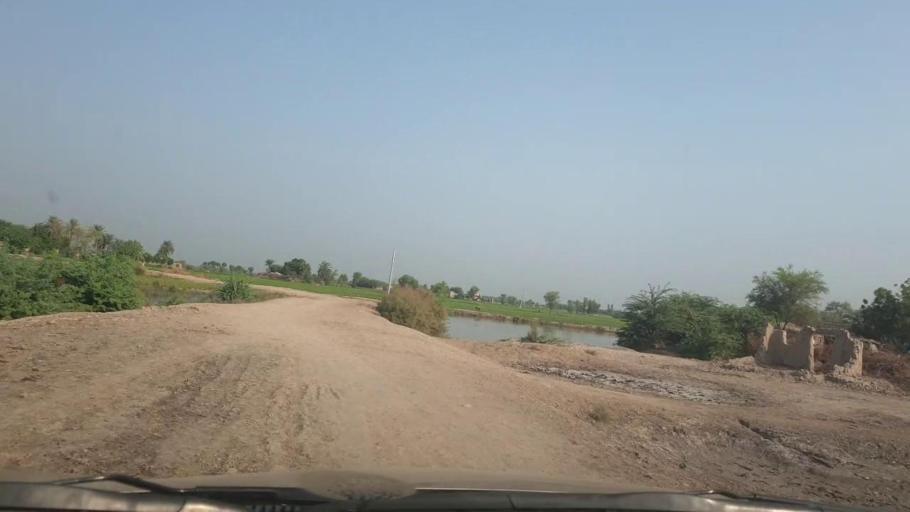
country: PK
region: Sindh
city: Larkana
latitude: 27.6000
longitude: 68.1601
